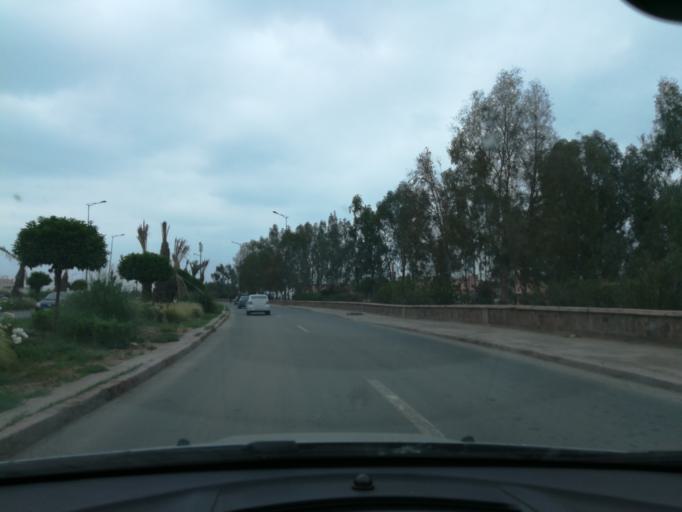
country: MA
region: Marrakech-Tensift-Al Haouz
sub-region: Marrakech
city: Marrakesh
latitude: 31.6607
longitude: -7.9847
